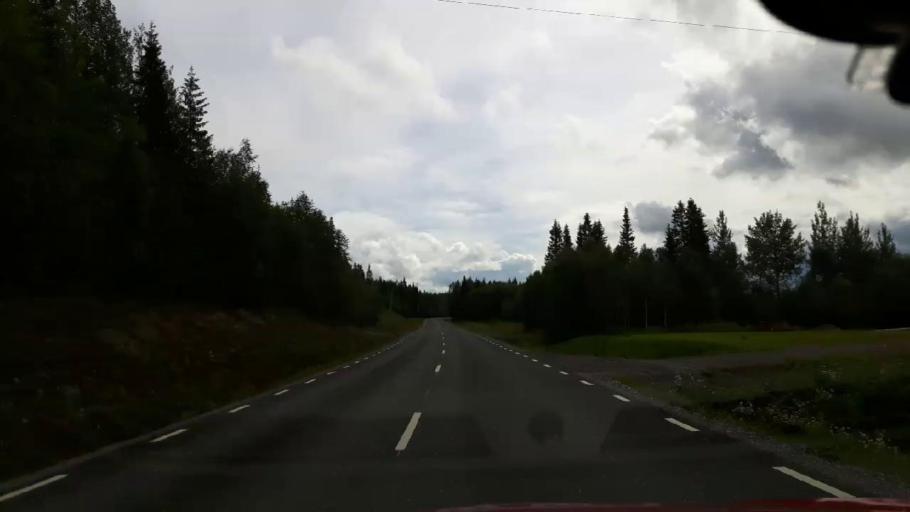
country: NO
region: Nord-Trondelag
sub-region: Lierne
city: Sandvika
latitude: 64.5896
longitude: 14.1183
